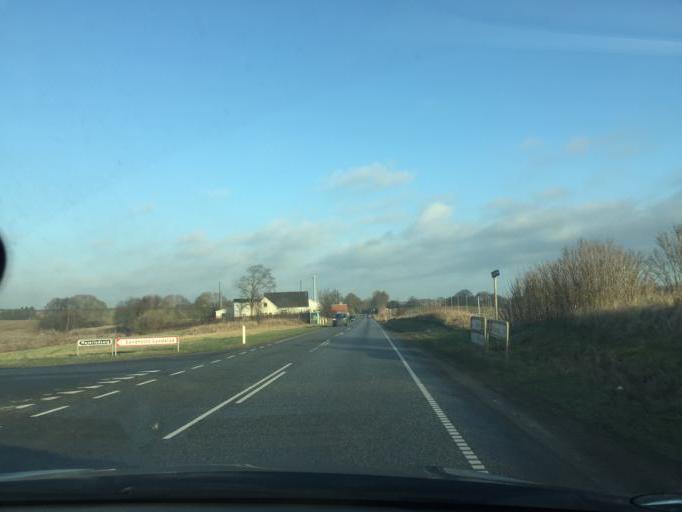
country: DK
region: South Denmark
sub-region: Faaborg-Midtfyn Kommune
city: Faaborg
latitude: 55.1952
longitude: 10.3173
